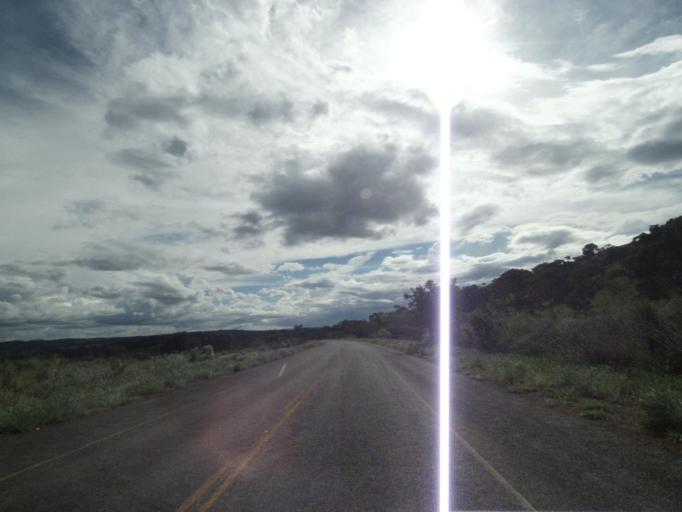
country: BR
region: Goias
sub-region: Jaragua
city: Jaragua
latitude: -15.8393
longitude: -49.3225
